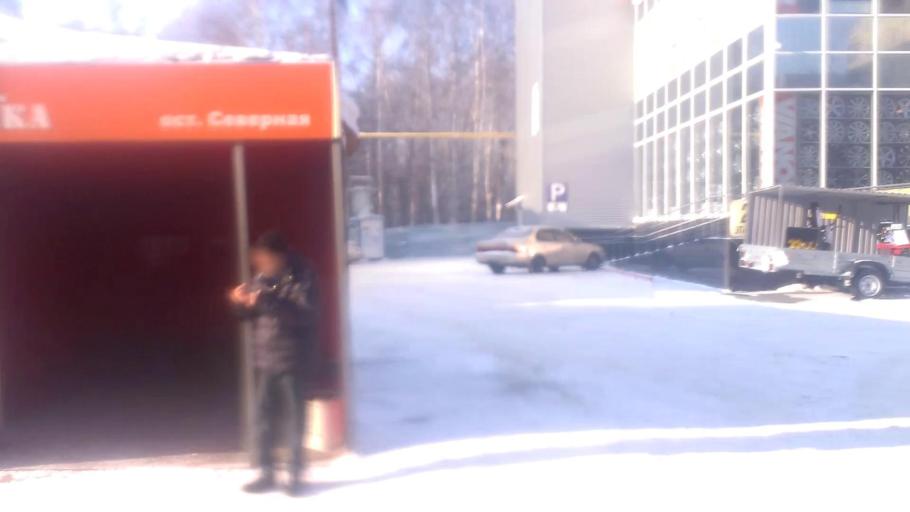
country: RU
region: Altai Krai
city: Novosilikatnyy
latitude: 53.3735
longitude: 83.6626
